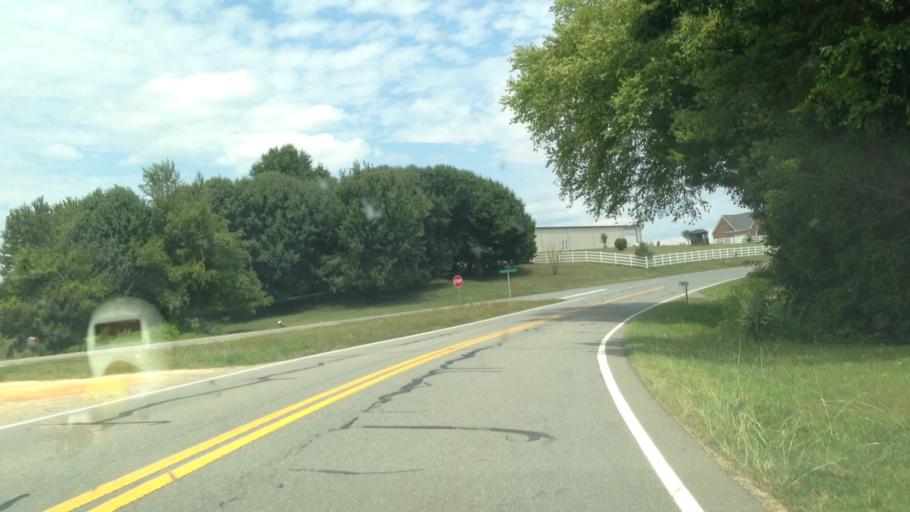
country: US
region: North Carolina
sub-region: Stokes County
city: Walnut Cove
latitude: 36.2787
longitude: -80.0876
